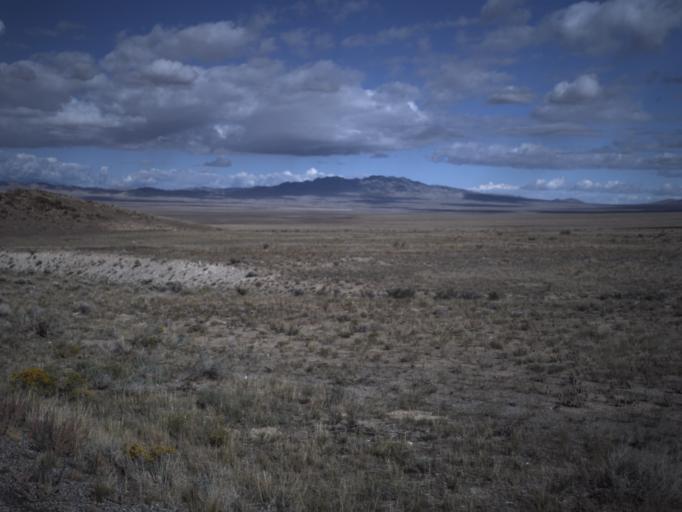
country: US
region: Utah
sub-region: Beaver County
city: Milford
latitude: 38.5081
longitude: -113.6165
